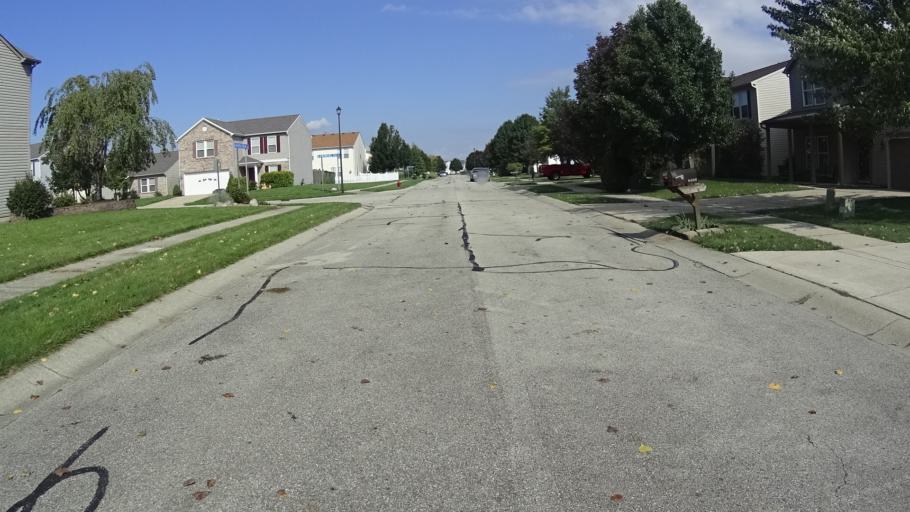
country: US
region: Indiana
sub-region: Madison County
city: Ingalls
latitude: 39.9806
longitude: -85.8460
